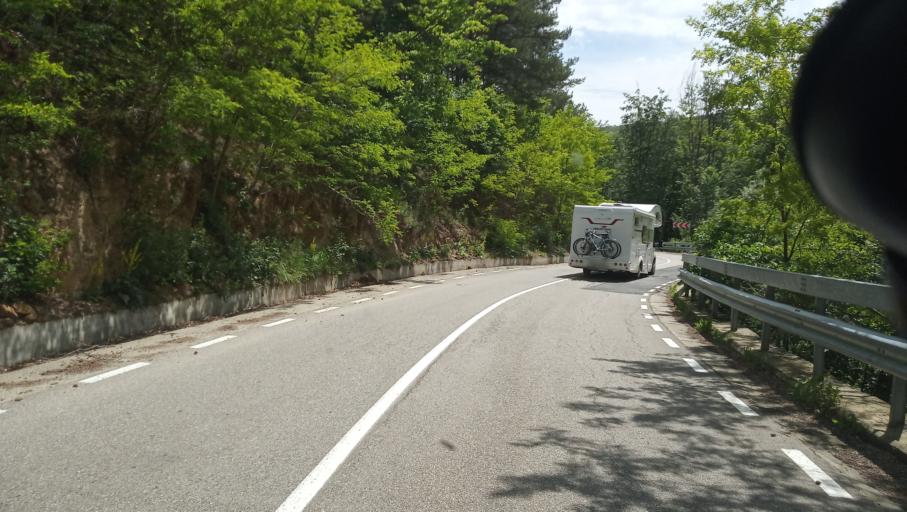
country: RO
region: Caras-Severin
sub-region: Comuna Brebu Nou
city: Brebu Nou
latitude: 45.2514
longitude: 22.1781
